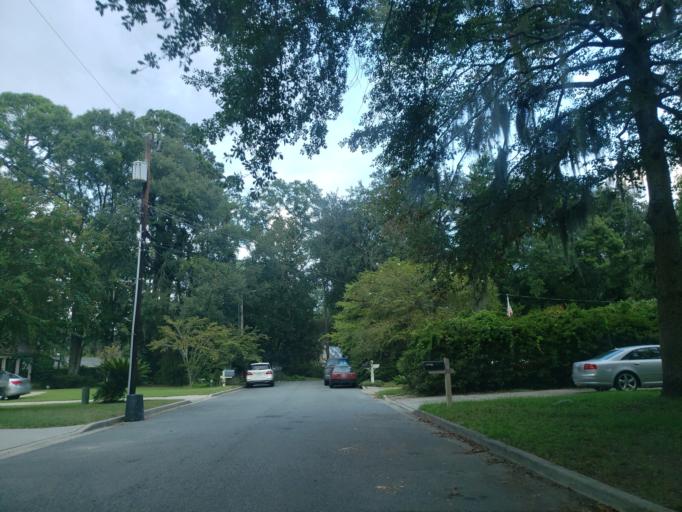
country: US
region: Georgia
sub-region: Chatham County
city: Isle of Hope
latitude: 31.9854
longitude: -81.0579
